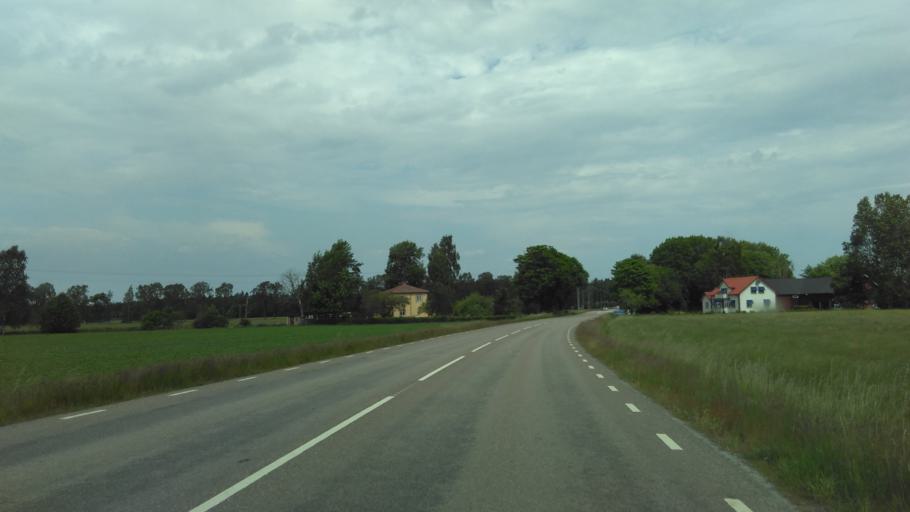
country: SE
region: Vaestra Goetaland
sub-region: Lidkopings Kommun
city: Lidkoping
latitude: 58.4784
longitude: 13.1367
